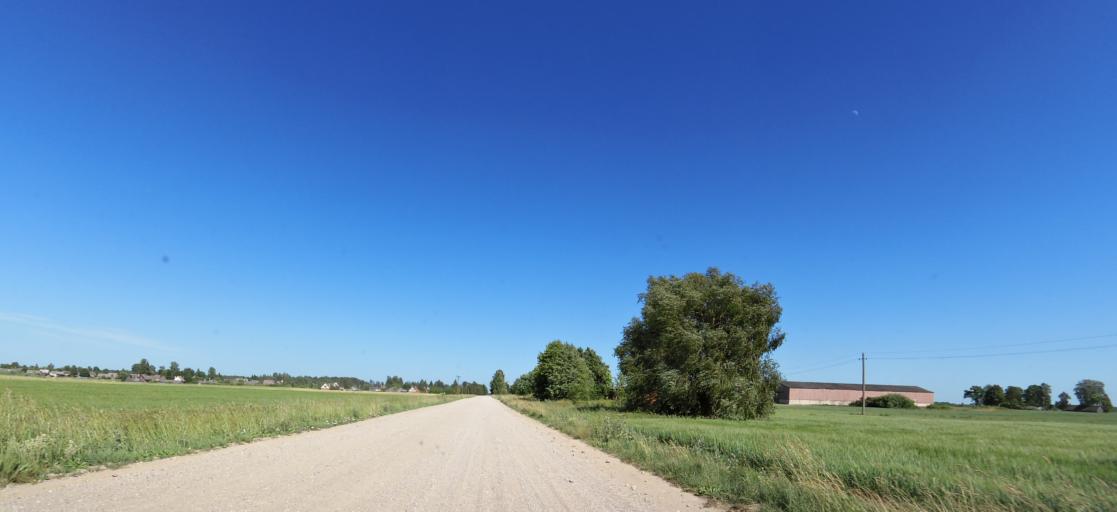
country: LT
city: Vabalninkas
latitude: 56.0270
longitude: 24.6460
